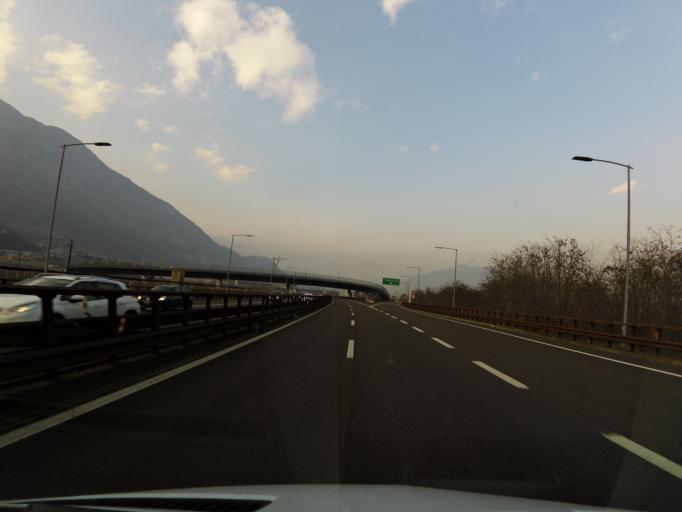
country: IT
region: Trentino-Alto Adige
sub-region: Provincia di Trento
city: Ravina
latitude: 46.0285
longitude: 11.1221
